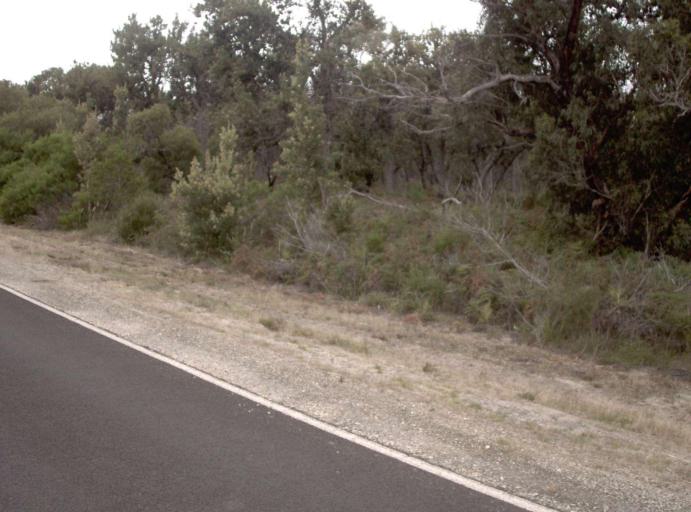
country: AU
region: Victoria
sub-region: East Gippsland
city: Bairnsdale
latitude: -38.0797
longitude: 147.5349
